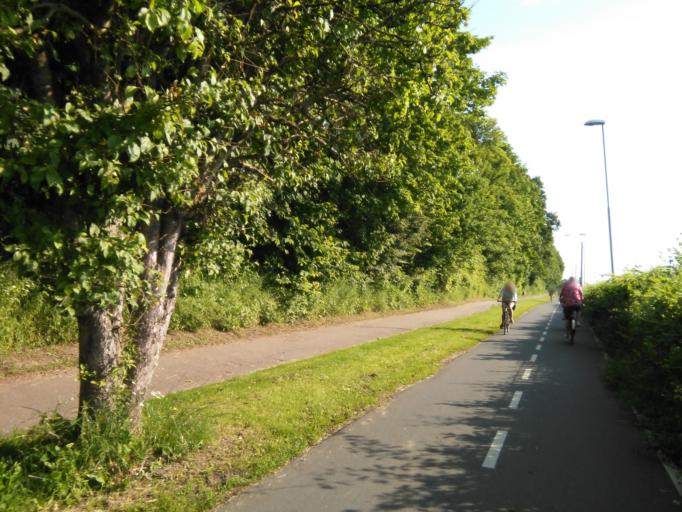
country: DK
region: Central Jutland
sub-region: Arhus Kommune
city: Arhus
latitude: 56.1714
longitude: 10.2244
